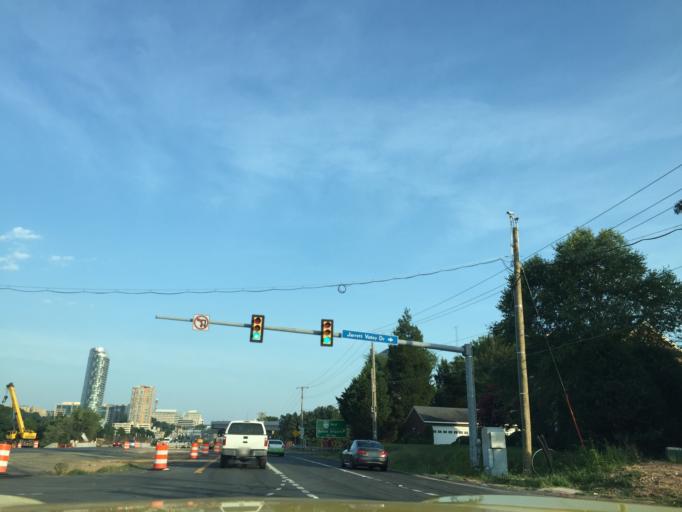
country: US
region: Virginia
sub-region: Fairfax County
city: Tysons Corner
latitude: 38.9356
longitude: -77.2482
